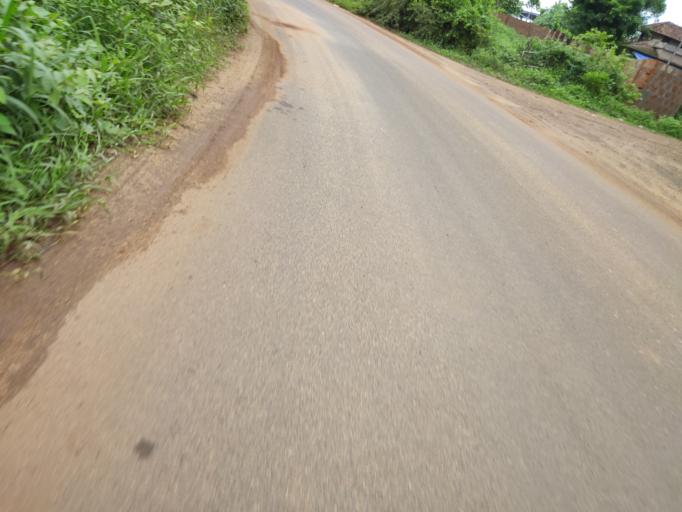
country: IN
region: Kerala
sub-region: Malappuram
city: Manjeri
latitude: 11.2209
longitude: 76.2622
